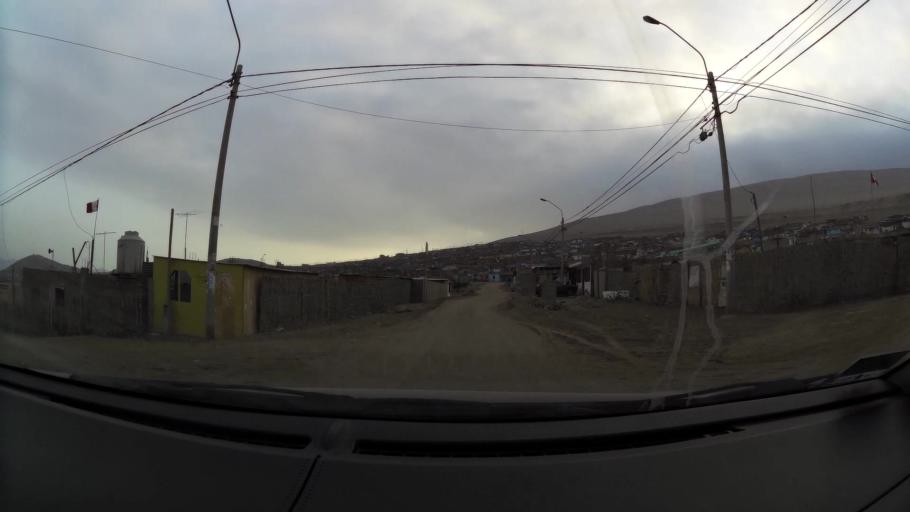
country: PE
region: Lima
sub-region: Lima
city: Santa Rosa
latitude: -11.7297
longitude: -77.1435
